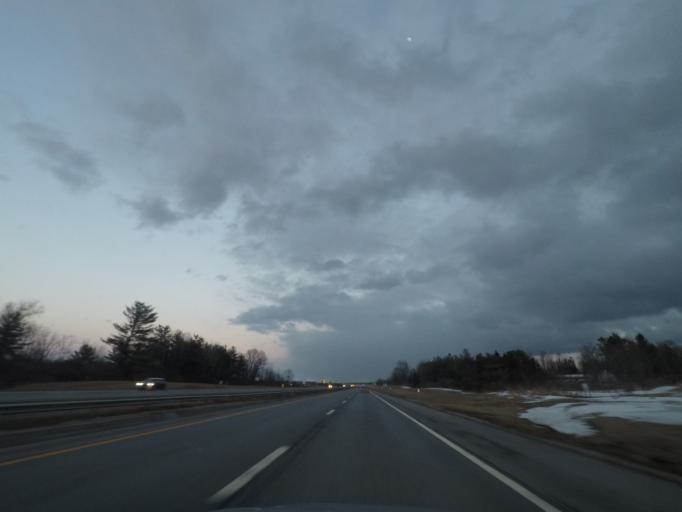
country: US
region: New York
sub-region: Montgomery County
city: Amsterdam
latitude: 42.9260
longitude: -74.2113
